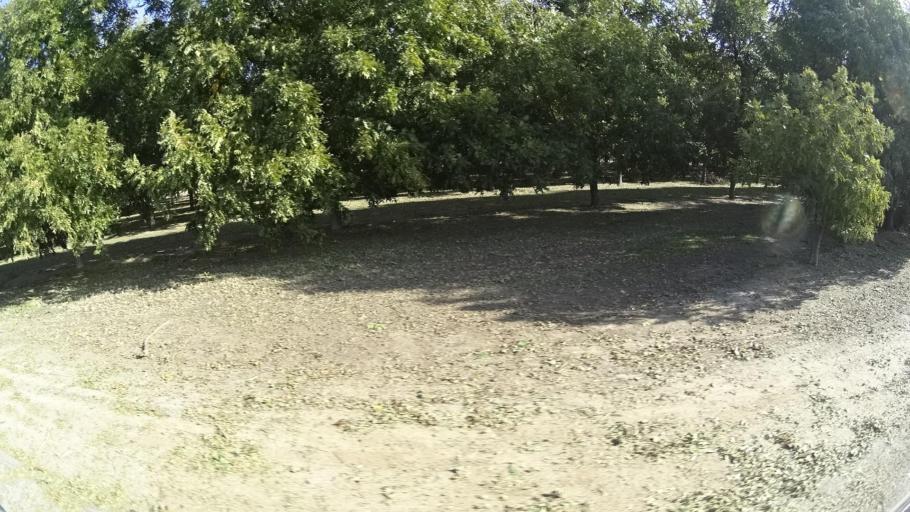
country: US
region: California
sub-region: Kern County
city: McFarland
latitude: 35.6344
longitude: -119.2054
